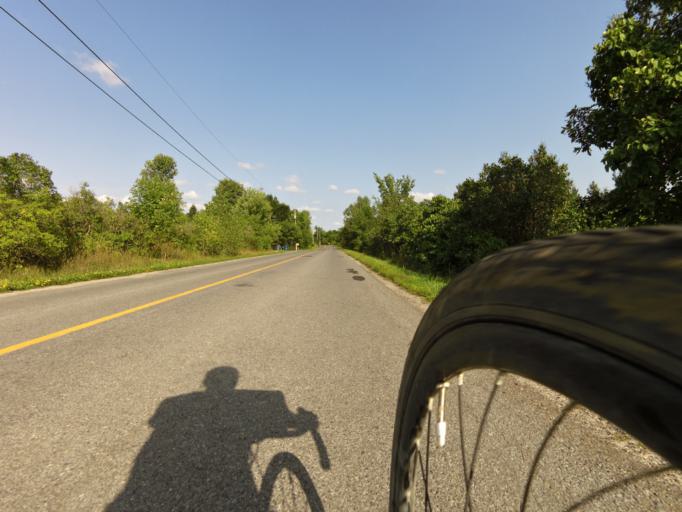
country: CA
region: Ontario
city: Kingston
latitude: 44.3692
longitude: -76.5979
